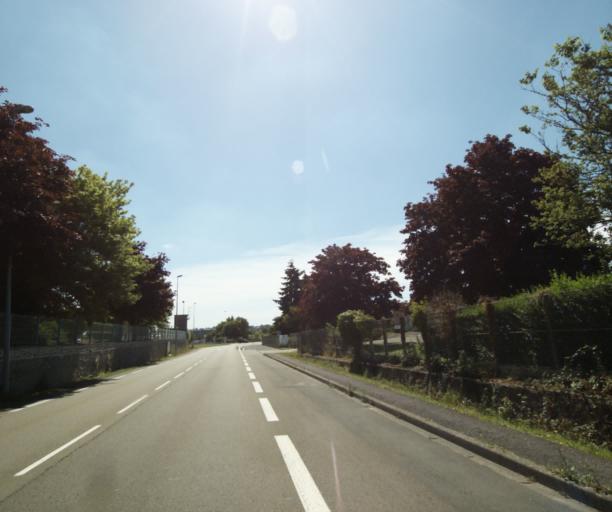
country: FR
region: Pays de la Loire
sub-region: Departement de la Mayenne
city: Laval
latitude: 48.0759
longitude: -0.7458
